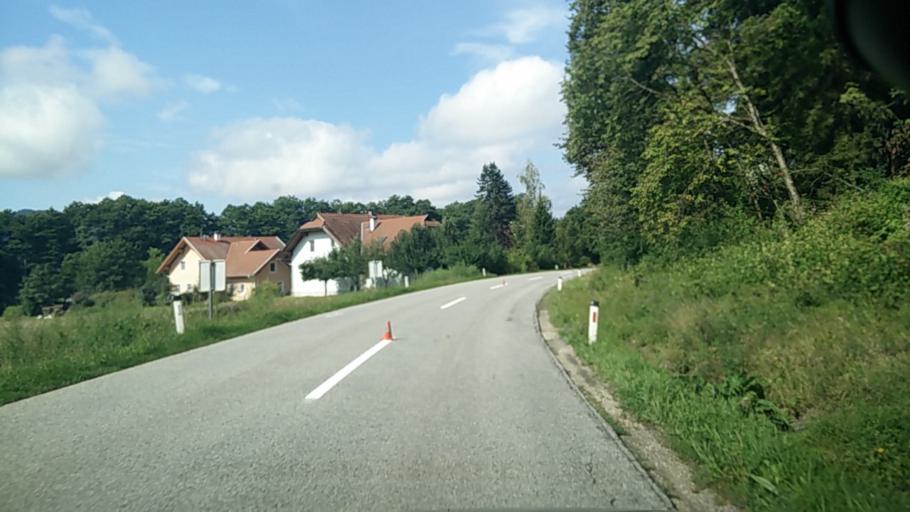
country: AT
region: Carinthia
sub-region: Politischer Bezirk Klagenfurt Land
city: Grafenstein
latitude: 46.6185
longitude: 14.5196
